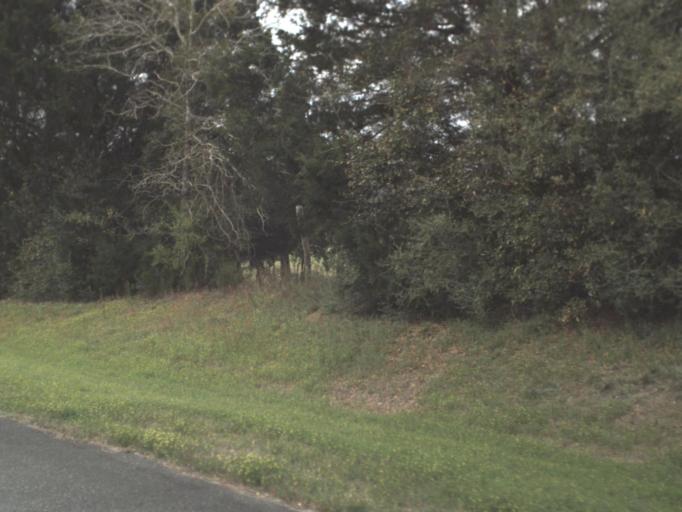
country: US
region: Florida
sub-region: Calhoun County
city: Blountstown
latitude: 30.5523
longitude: -85.1869
